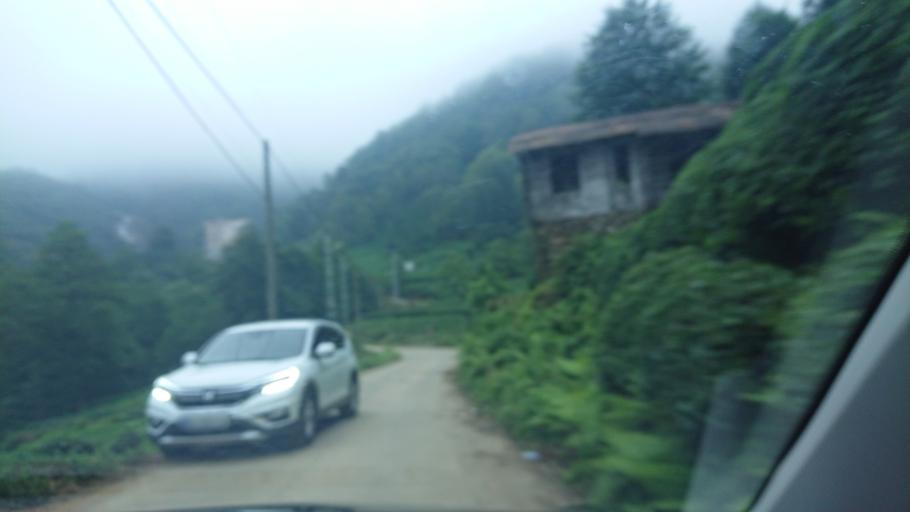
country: TR
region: Rize
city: Kaptanpasa
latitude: 41.0457
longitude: 40.8037
